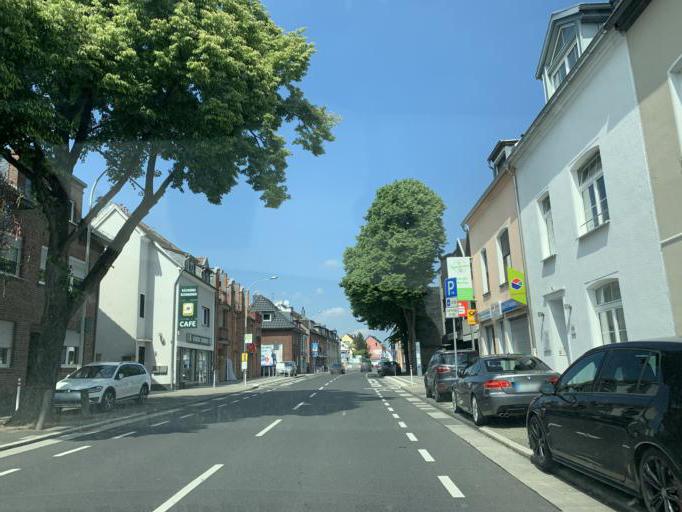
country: DE
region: North Rhine-Westphalia
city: Bruhl
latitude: 50.8142
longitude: 6.8888
